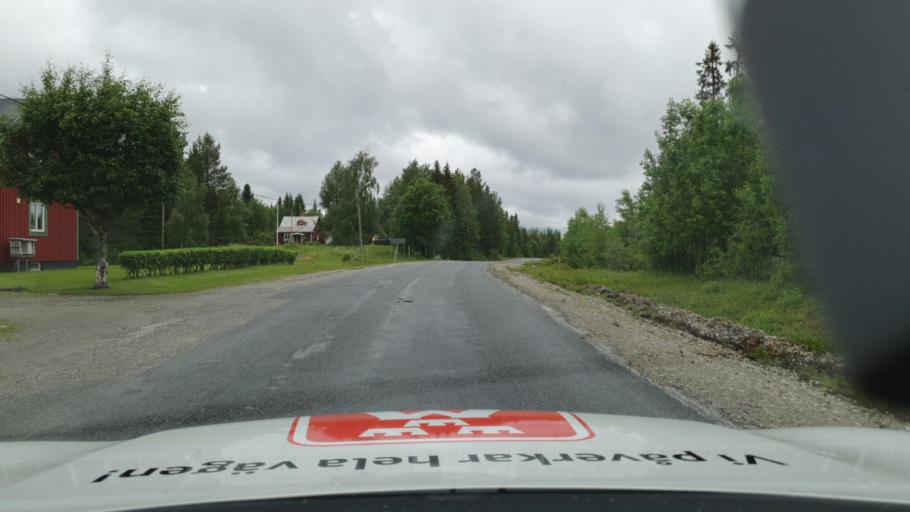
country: SE
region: Vaesterbotten
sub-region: Dorotea Kommun
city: Dorotea
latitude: 64.1154
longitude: 16.6346
